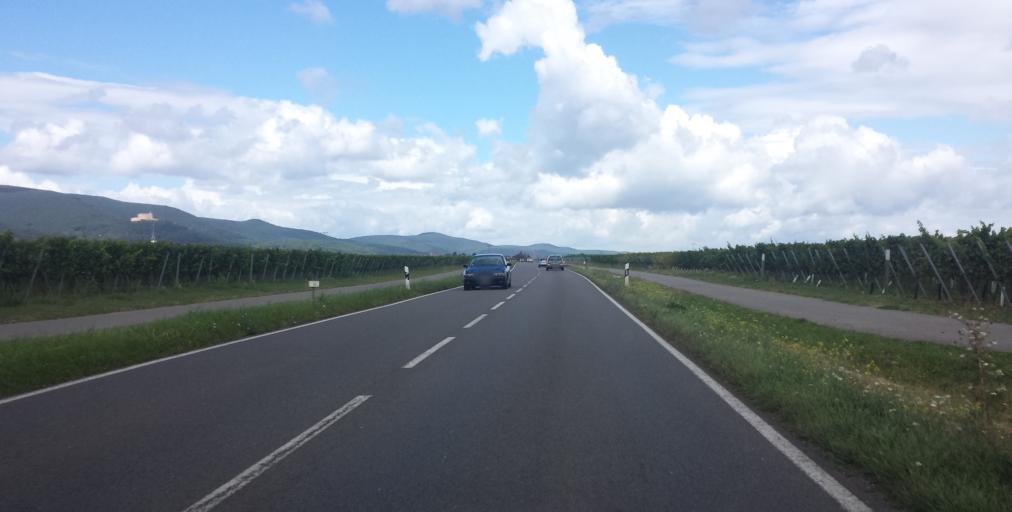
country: DE
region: Rheinland-Pfalz
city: Edenkoben
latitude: 49.2921
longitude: 8.1406
